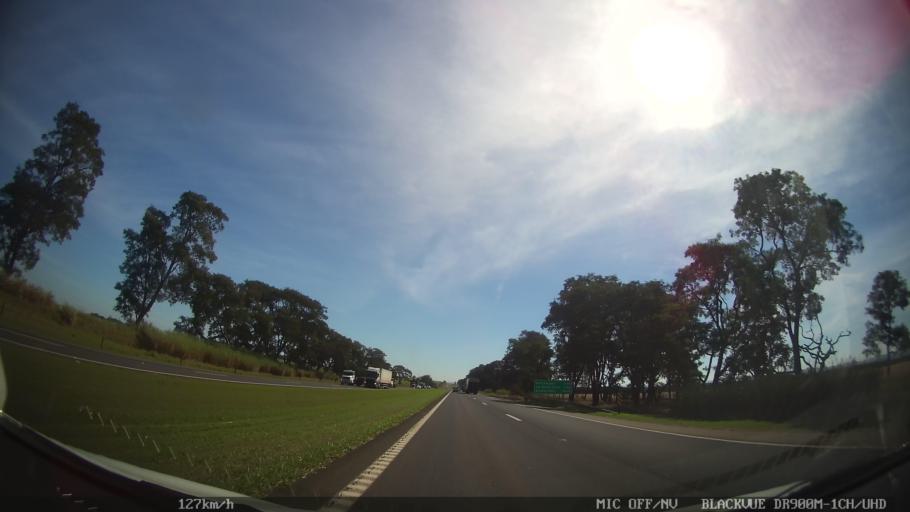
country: BR
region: Sao Paulo
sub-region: Porto Ferreira
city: Porto Ferreira
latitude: -21.9004
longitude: -47.4790
